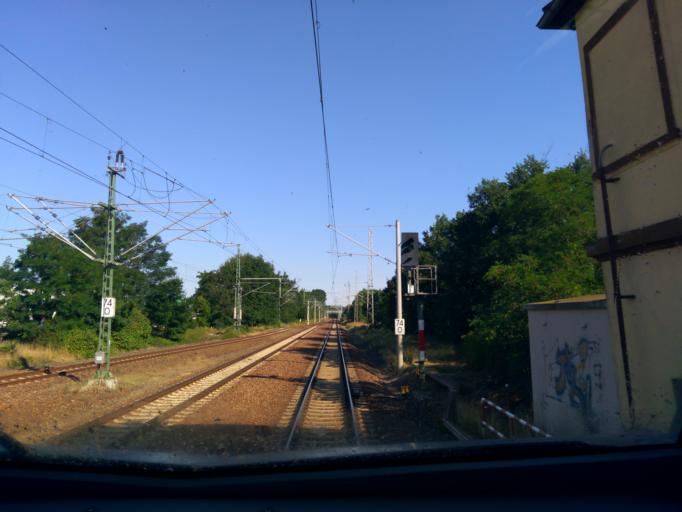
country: DE
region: Brandenburg
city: Luebben
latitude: 51.9436
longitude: 13.8711
